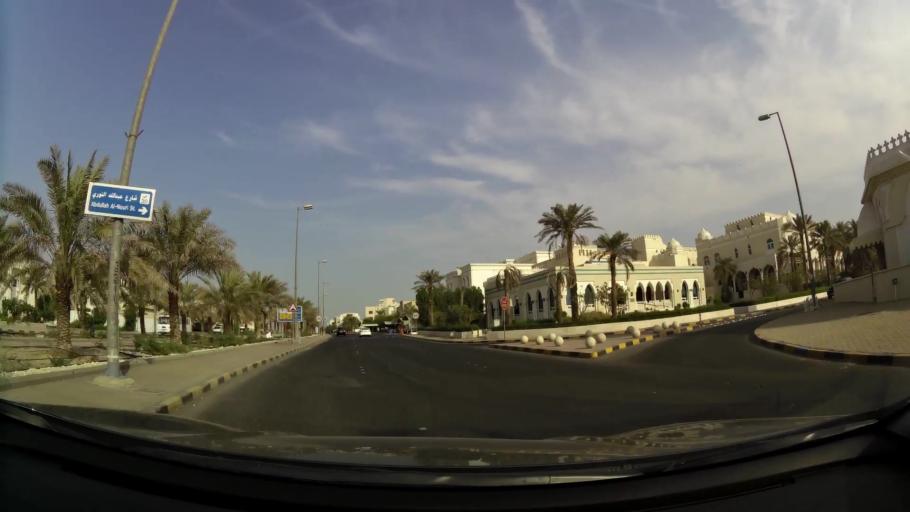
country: KW
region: Al Asimah
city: Ash Shamiyah
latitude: 29.3245
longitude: 47.9737
